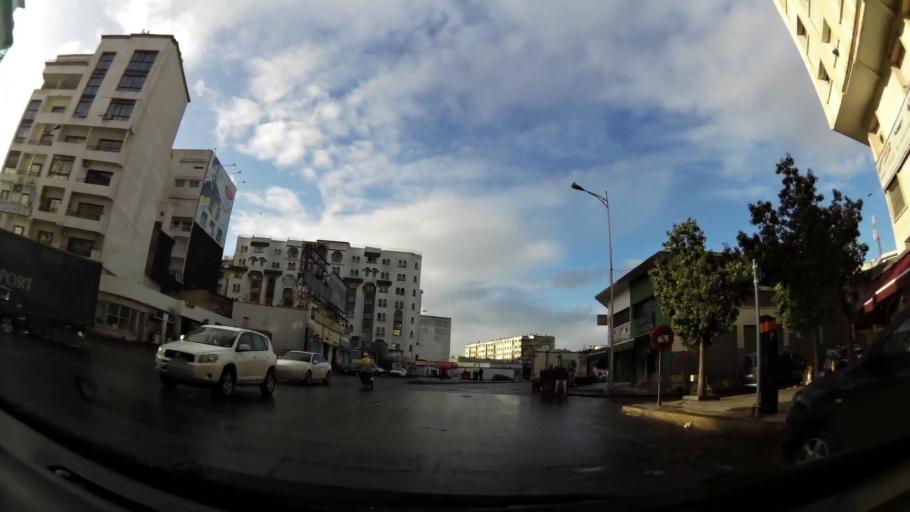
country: MA
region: Grand Casablanca
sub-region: Casablanca
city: Casablanca
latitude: 33.5900
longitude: -7.6085
